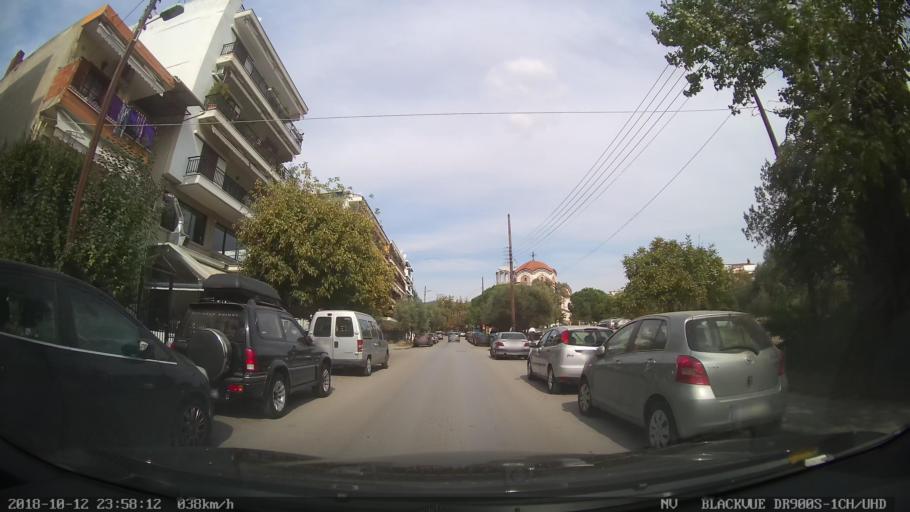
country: GR
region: Central Macedonia
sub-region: Nomos Thessalonikis
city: Pylaia
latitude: 40.6081
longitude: 22.9867
